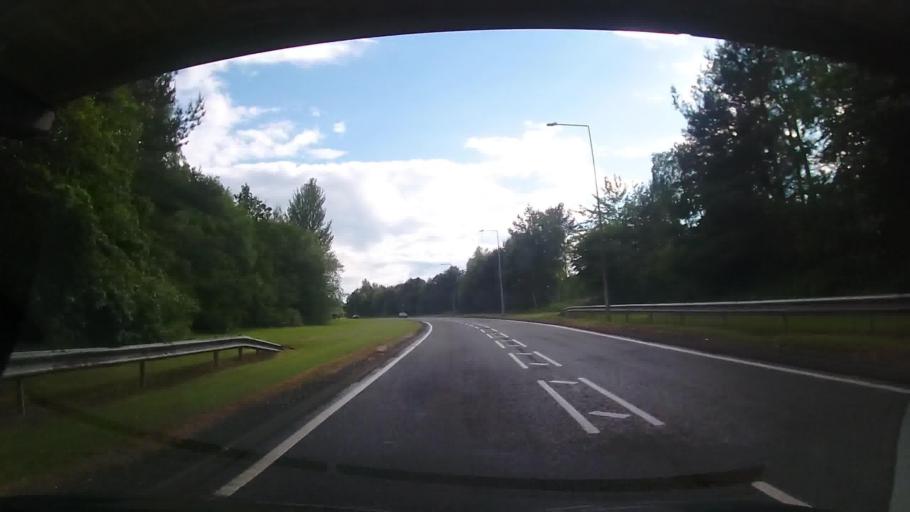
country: GB
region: England
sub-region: Telford and Wrekin
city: Telford
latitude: 52.6801
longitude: -2.4651
